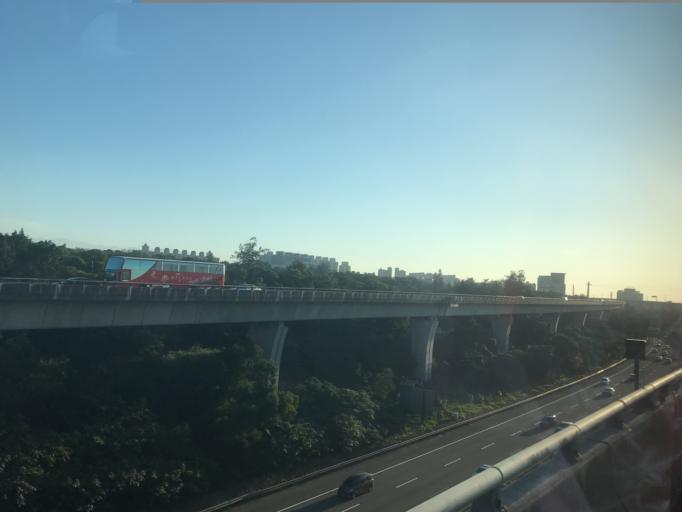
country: TW
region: Taiwan
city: Daxi
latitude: 24.9309
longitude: 121.1797
